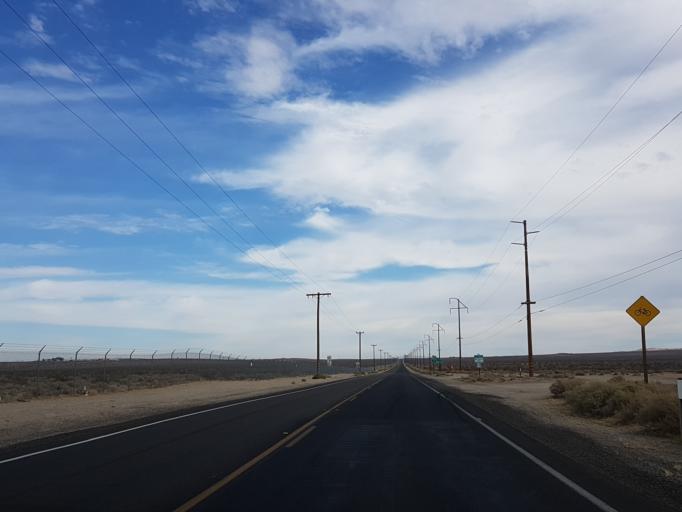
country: US
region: California
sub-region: Kern County
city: Ridgecrest
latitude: 35.6225
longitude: -117.6342
